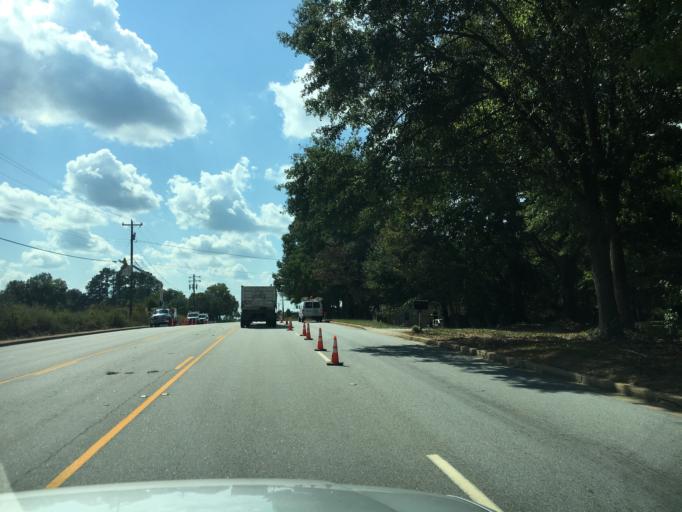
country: US
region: South Carolina
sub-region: Spartanburg County
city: Woodruff
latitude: 34.7554
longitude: -82.0405
